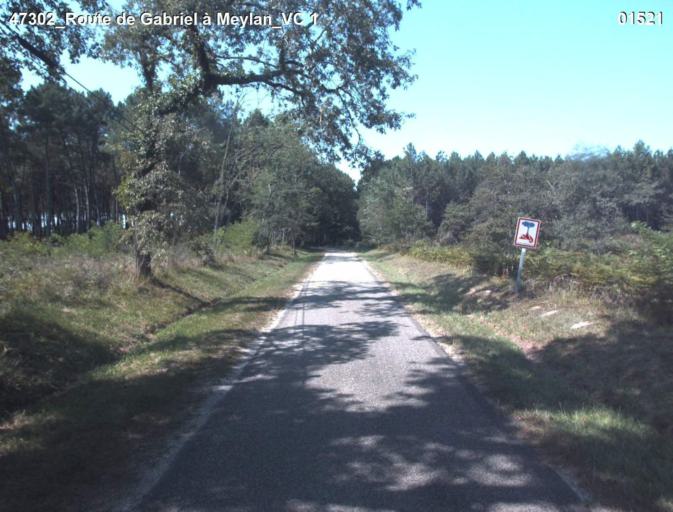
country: FR
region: Aquitaine
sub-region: Departement du Lot-et-Garonne
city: Mezin
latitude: 44.0649
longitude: 0.1411
